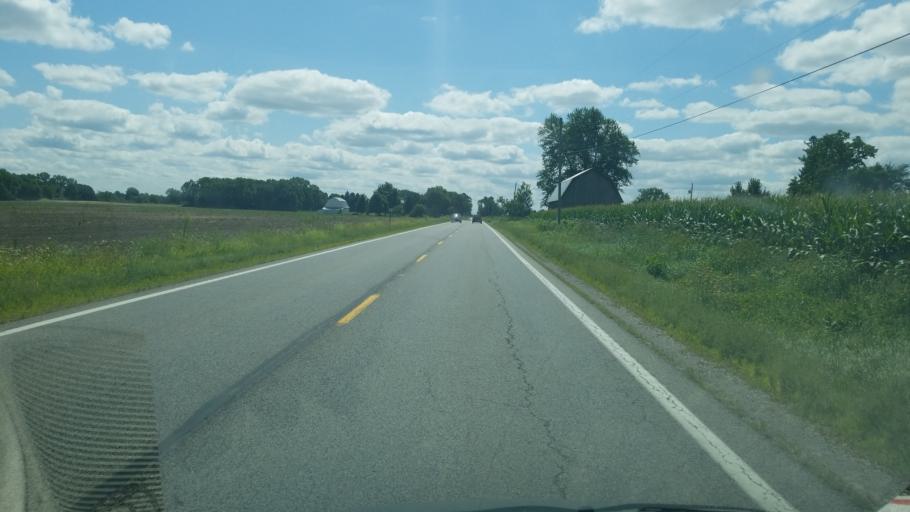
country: US
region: Ohio
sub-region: Fulton County
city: Delta
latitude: 41.6167
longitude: -84.0375
